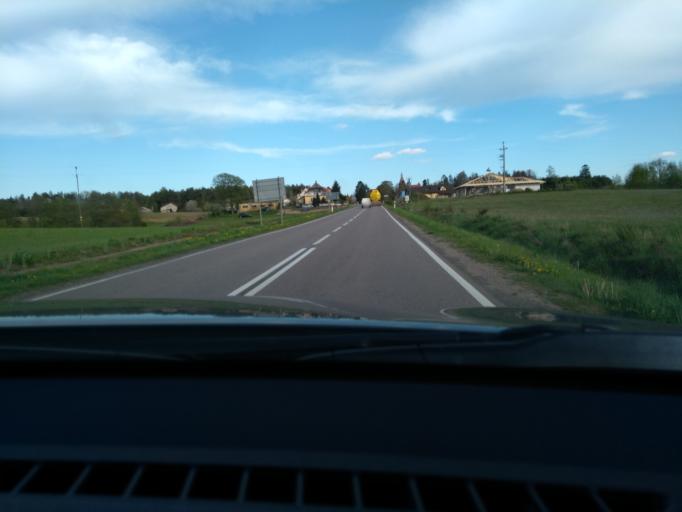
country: PL
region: Pomeranian Voivodeship
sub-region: Powiat leborski
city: Cewice
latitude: 54.3417
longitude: 17.6821
